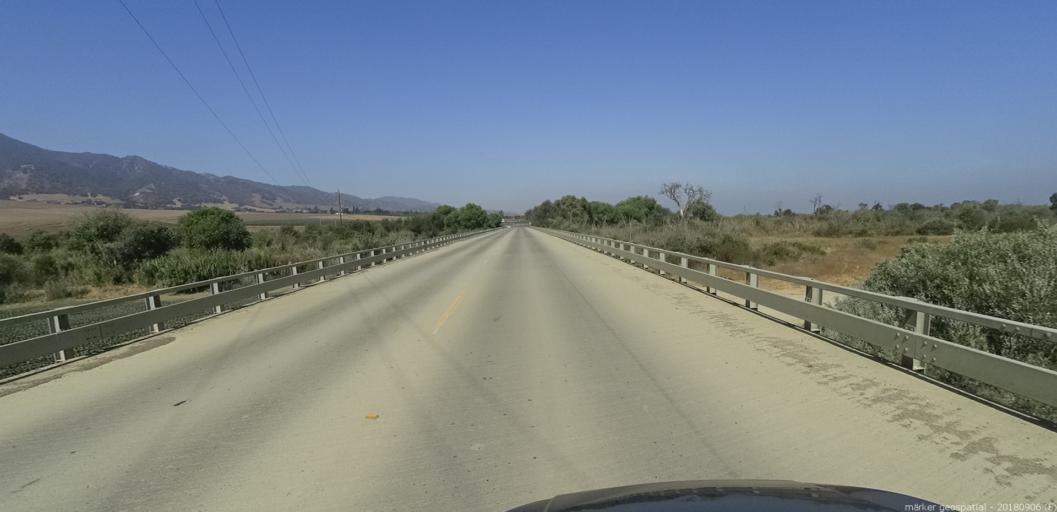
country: US
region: California
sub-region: Monterey County
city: Chualar
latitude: 36.5550
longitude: -121.5468
